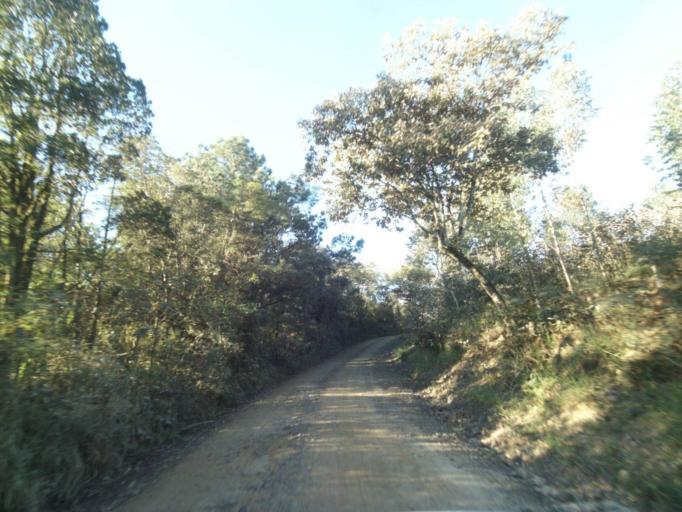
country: BR
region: Parana
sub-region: Tibagi
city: Tibagi
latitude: -24.5298
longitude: -50.5981
